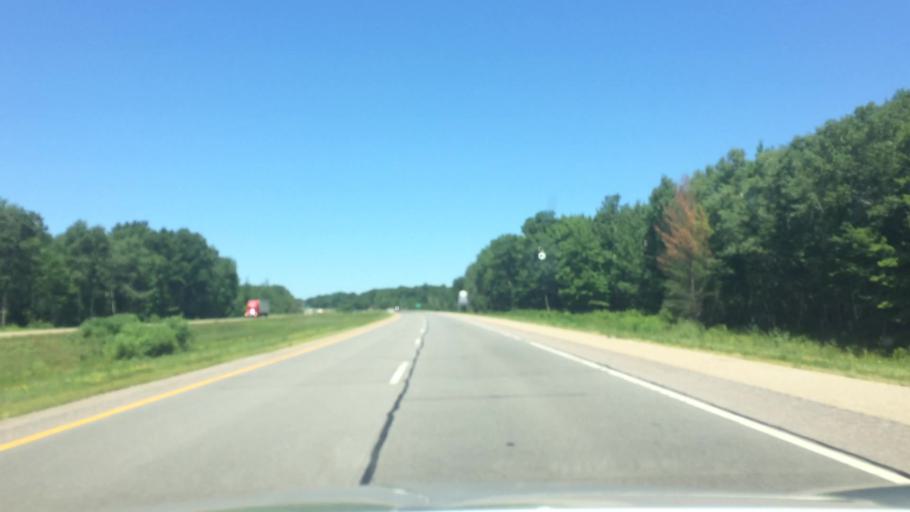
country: US
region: Wisconsin
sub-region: Marathon County
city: Mosinee
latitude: 44.7147
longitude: -89.6606
